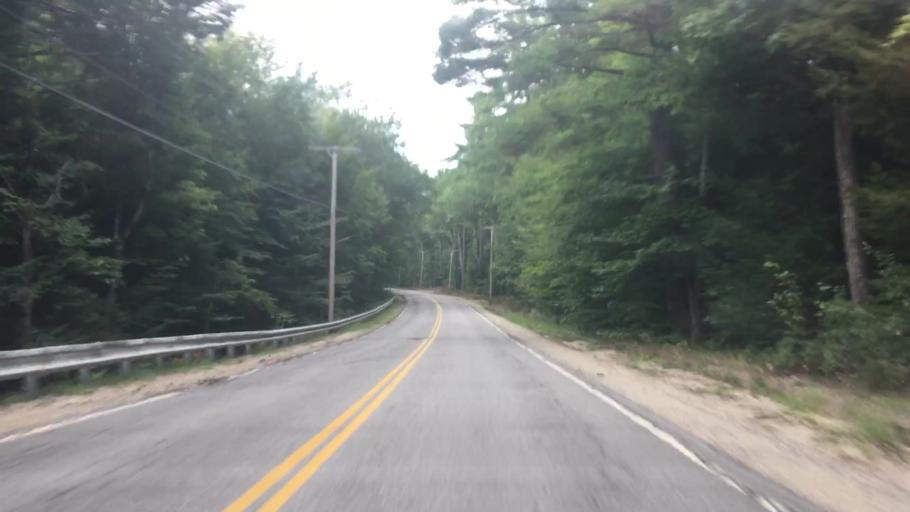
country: US
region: Maine
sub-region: Oxford County
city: Oxford
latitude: 44.0289
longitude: -70.5311
